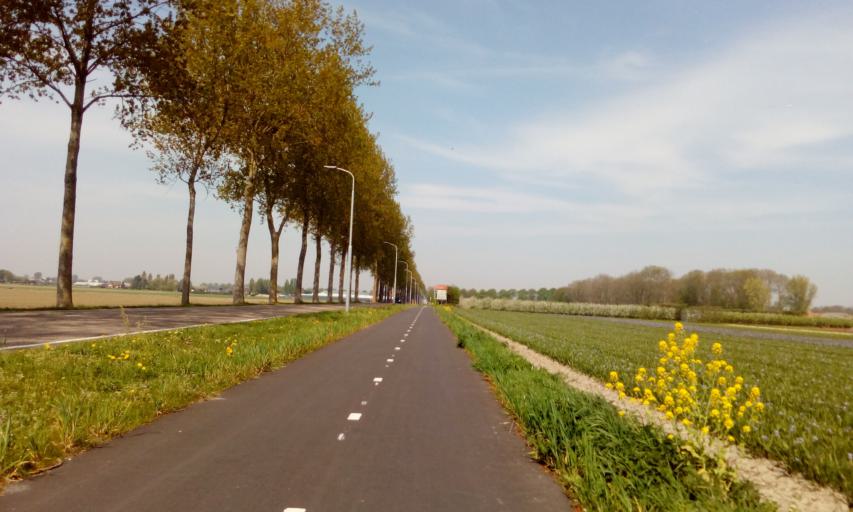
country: NL
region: South Holland
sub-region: Gemeente Lisse
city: Lisse
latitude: 52.2496
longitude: 4.5952
